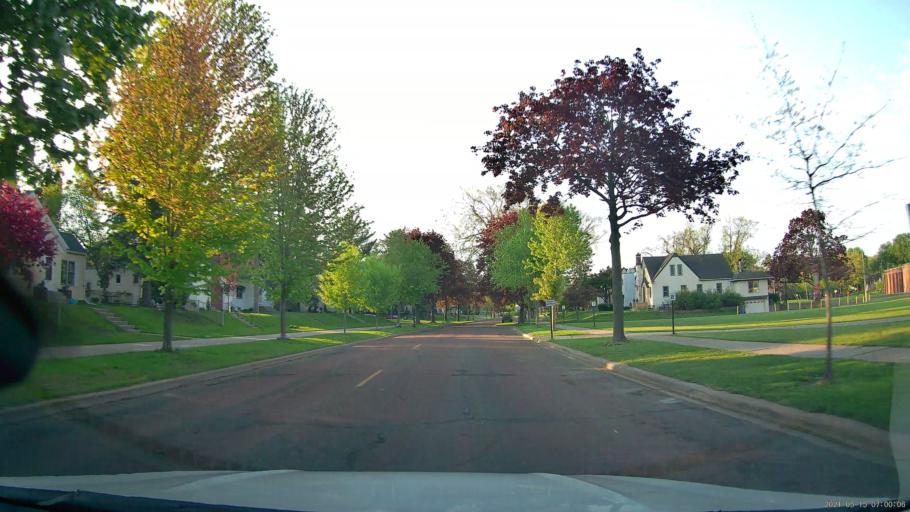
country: US
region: Minnesota
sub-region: Hennepin County
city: Saint Anthony
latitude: 45.0220
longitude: -93.2331
